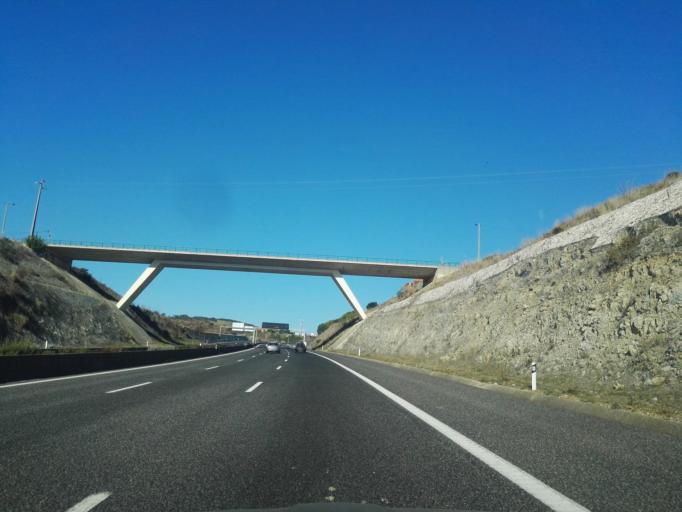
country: PT
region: Lisbon
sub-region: Vila Franca de Xira
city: Sobralinho
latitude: 38.9175
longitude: -9.0733
